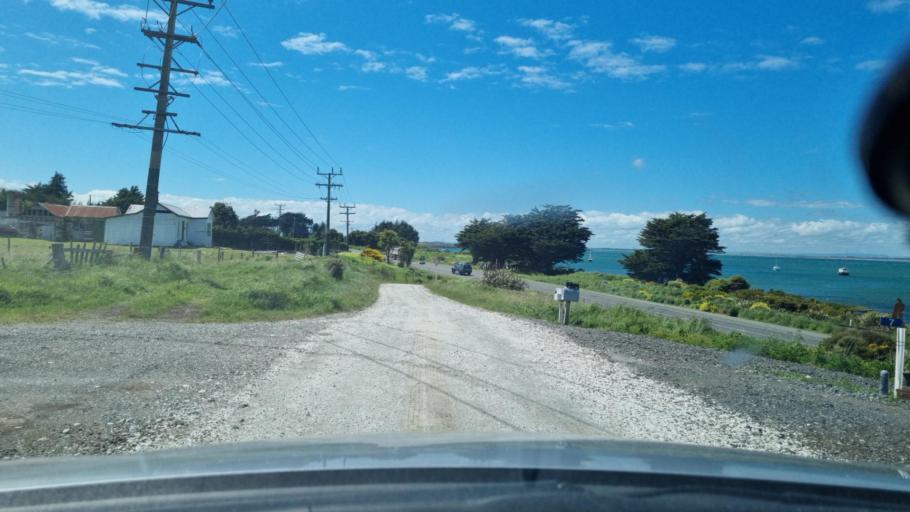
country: NZ
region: Southland
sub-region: Invercargill City
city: Bluff
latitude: -46.5849
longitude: 168.3043
